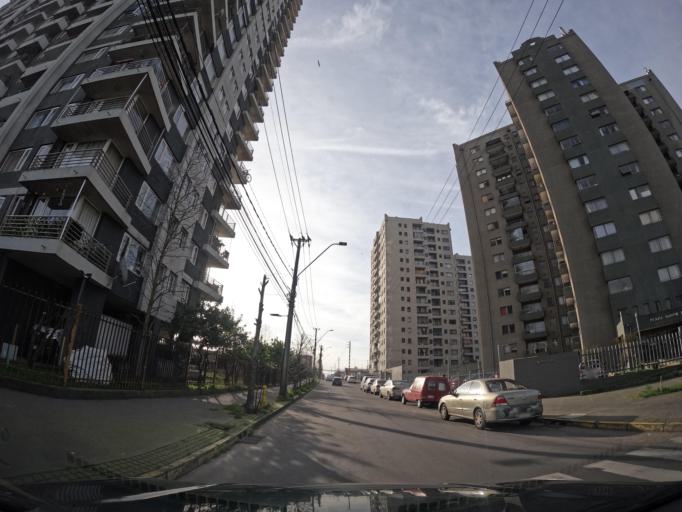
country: CL
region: Biobio
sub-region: Provincia de Concepcion
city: Concepcion
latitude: -36.8175
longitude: -73.0539
